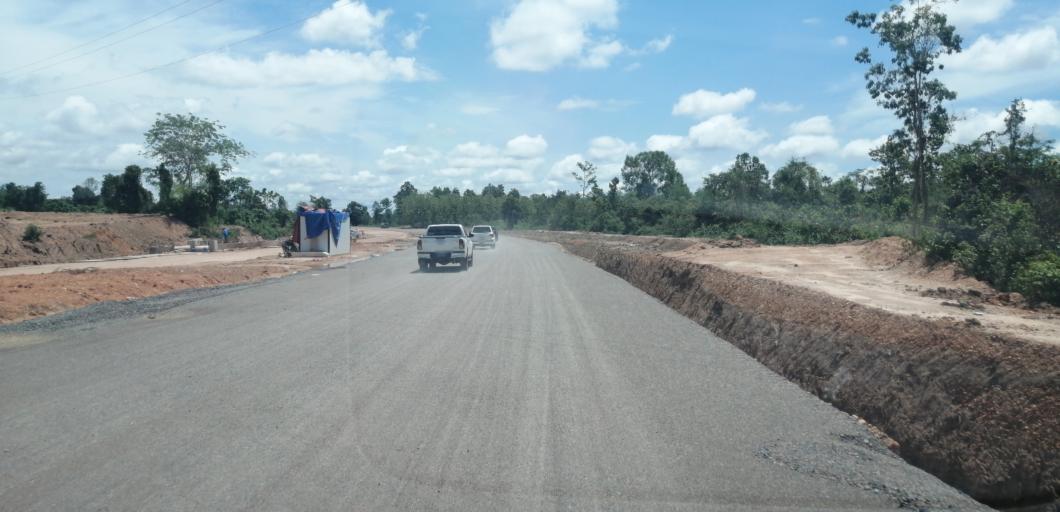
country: TH
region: Nong Khai
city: Sangkhom
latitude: 18.2270
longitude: 102.4821
